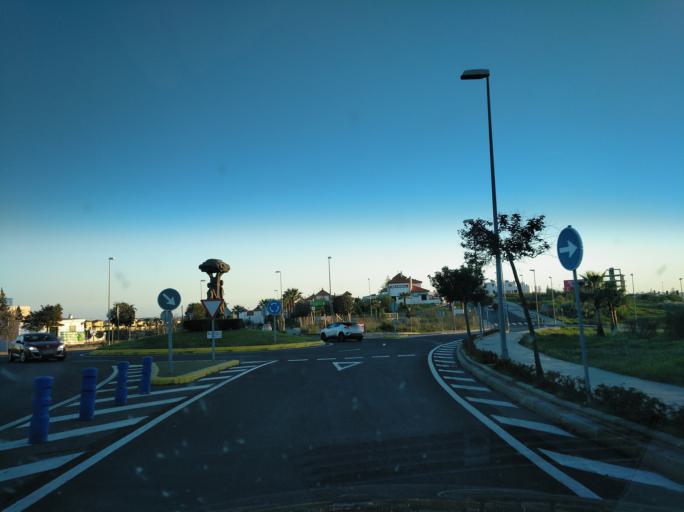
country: ES
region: Andalusia
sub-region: Provincia de Huelva
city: Ayamonte
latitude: 37.2230
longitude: -7.4014
